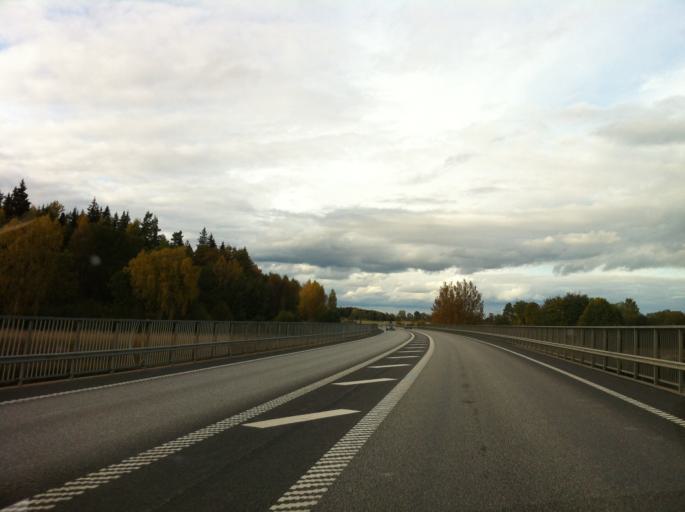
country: SE
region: OErebro
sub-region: Askersunds Kommun
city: Askersund
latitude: 58.8340
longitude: 14.9297
